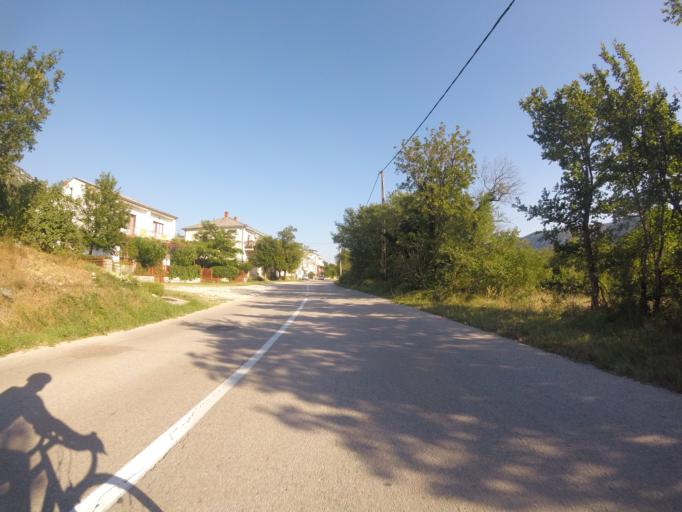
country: HR
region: Primorsko-Goranska
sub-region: Grad Crikvenica
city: Jadranovo
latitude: 45.2320
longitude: 14.6637
